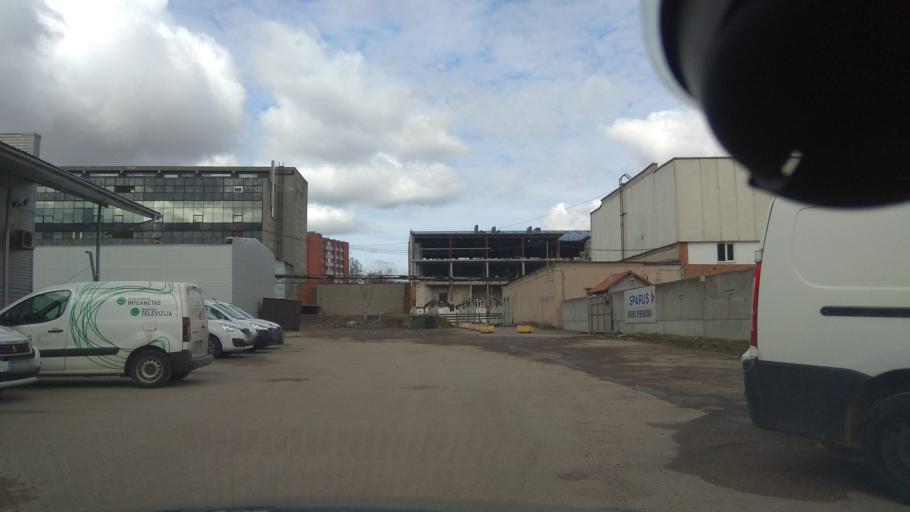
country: LT
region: Vilnius County
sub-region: Vilnius
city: Fabijoniskes
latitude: 54.7363
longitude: 25.2704
